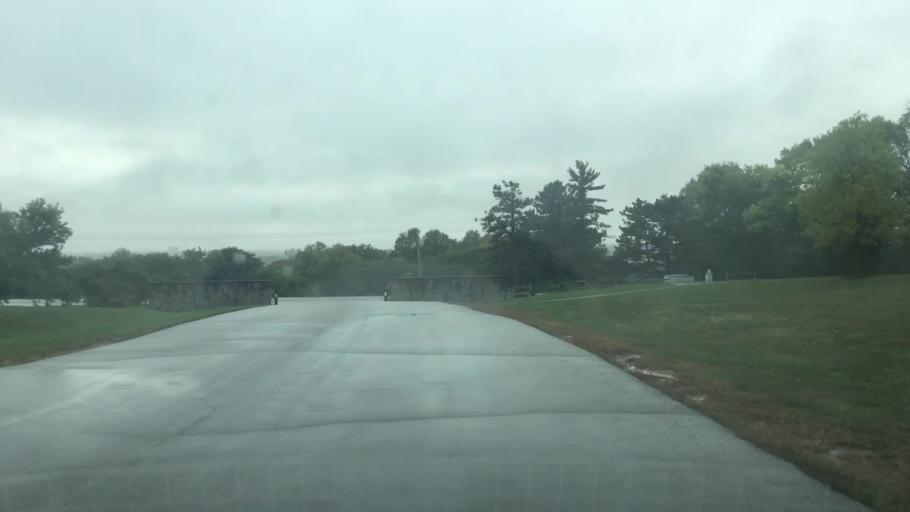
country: US
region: Kansas
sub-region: Johnson County
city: Lenexa
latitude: 38.9719
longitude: -94.8016
